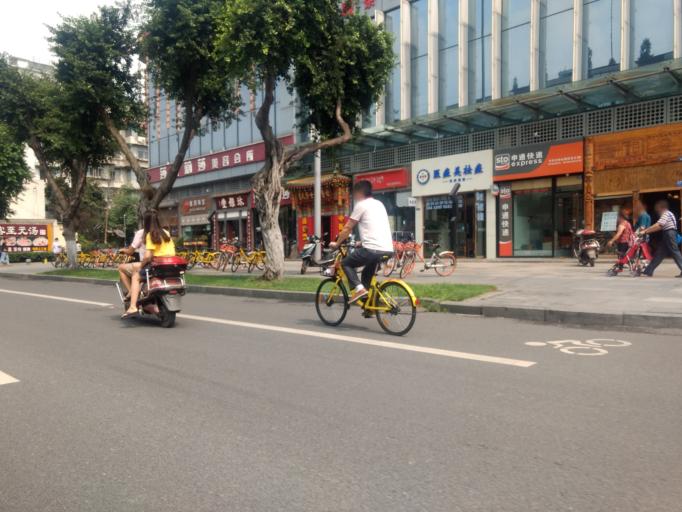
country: CN
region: Sichuan
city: Chengdu
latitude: 30.6631
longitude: 104.0358
